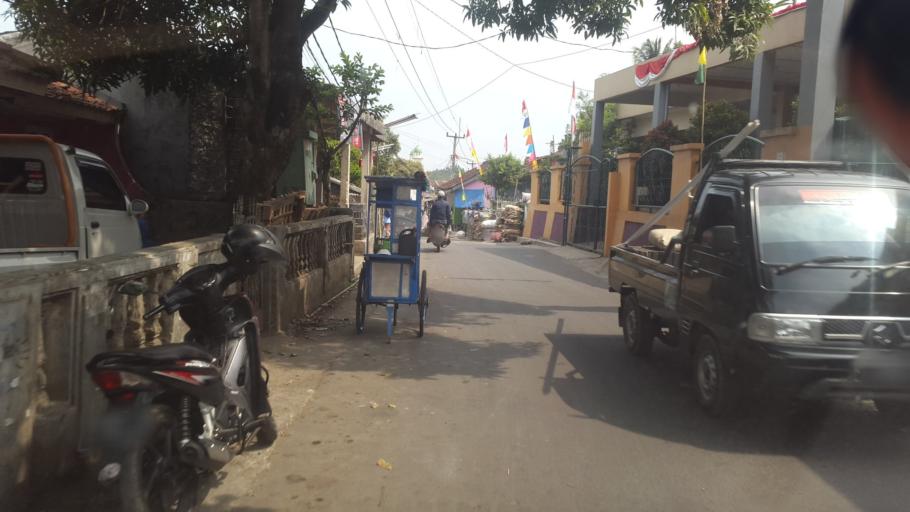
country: ID
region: West Java
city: Cicurug
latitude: -6.7603
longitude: 106.7687
